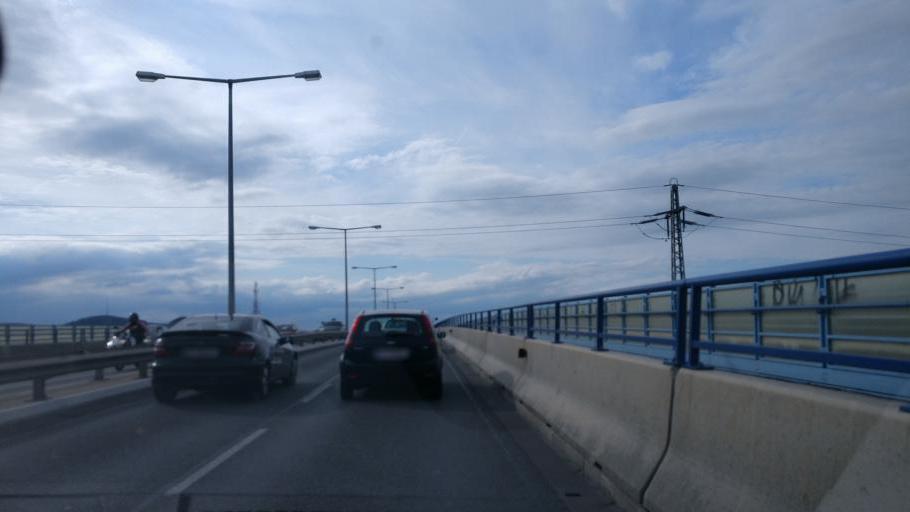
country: AT
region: Vienna
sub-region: Wien Stadt
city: Vienna
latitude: 48.2625
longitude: 16.4085
